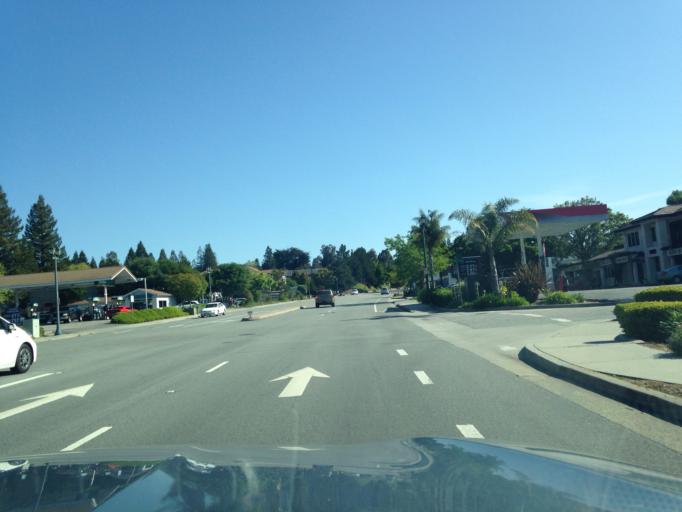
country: US
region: California
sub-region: Santa Cruz County
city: Scotts Valley
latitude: 37.0589
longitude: -122.0100
